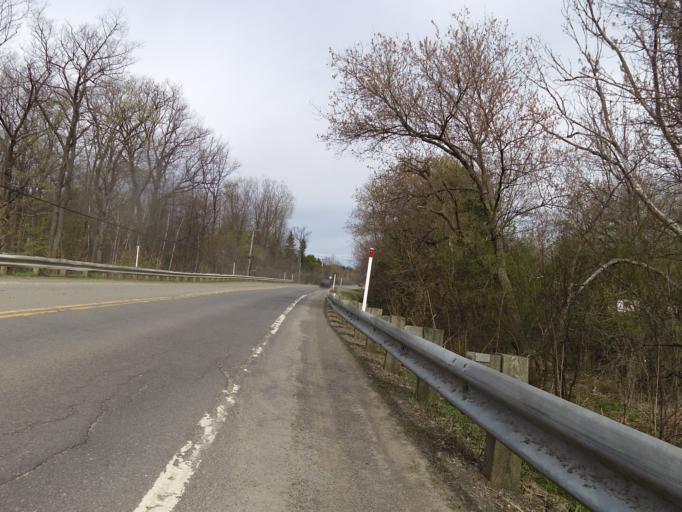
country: CA
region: Quebec
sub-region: Laurentides
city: Oka
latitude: 45.4673
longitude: -74.1144
